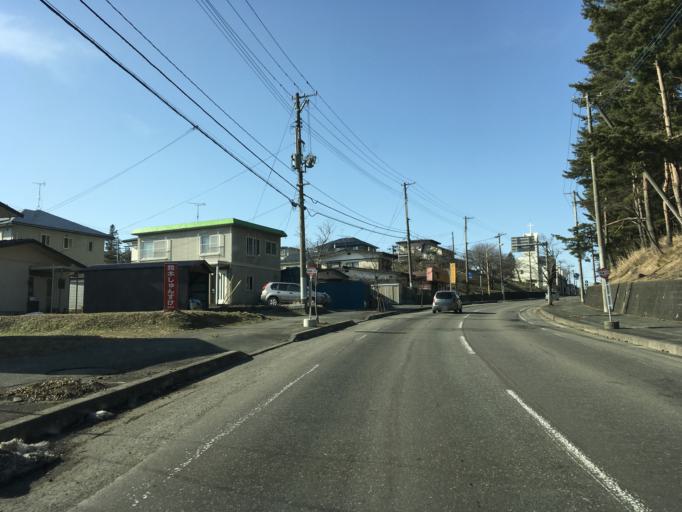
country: JP
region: Iwate
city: Morioka-shi
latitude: 39.7504
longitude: 141.1580
